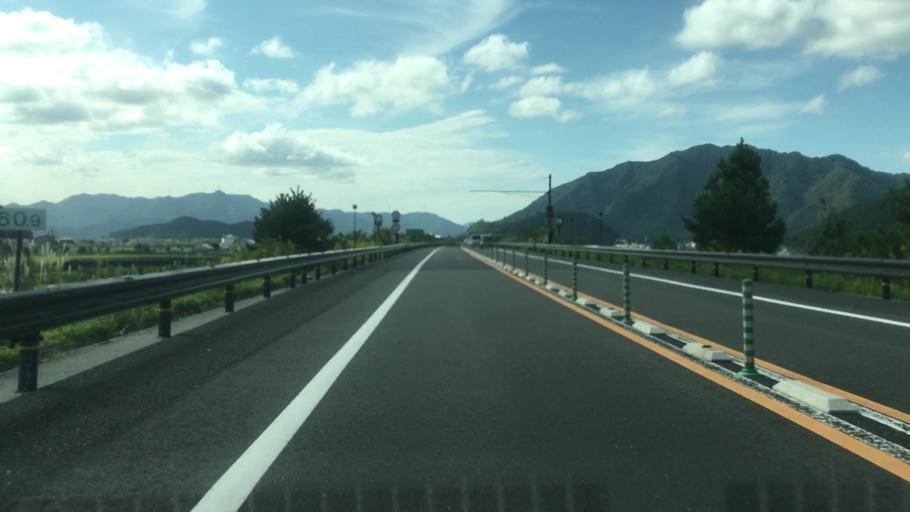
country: JP
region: Kyoto
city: Fukuchiyama
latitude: 35.1914
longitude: 135.0419
